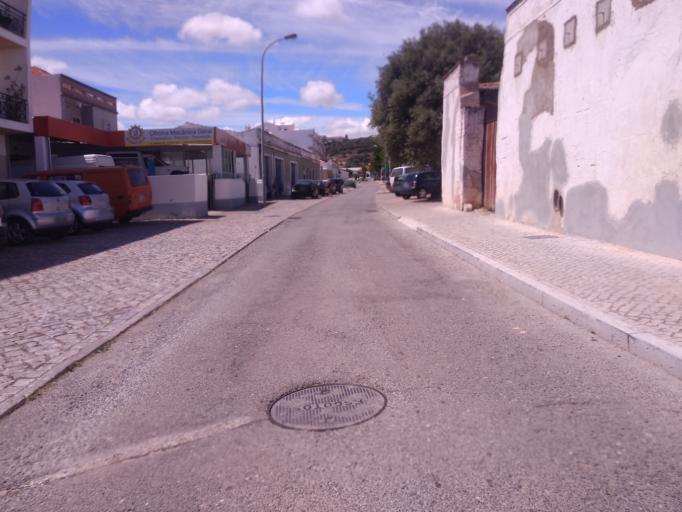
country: PT
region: Faro
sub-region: Sao Bras de Alportel
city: Sao Bras de Alportel
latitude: 37.1546
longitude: -7.8907
